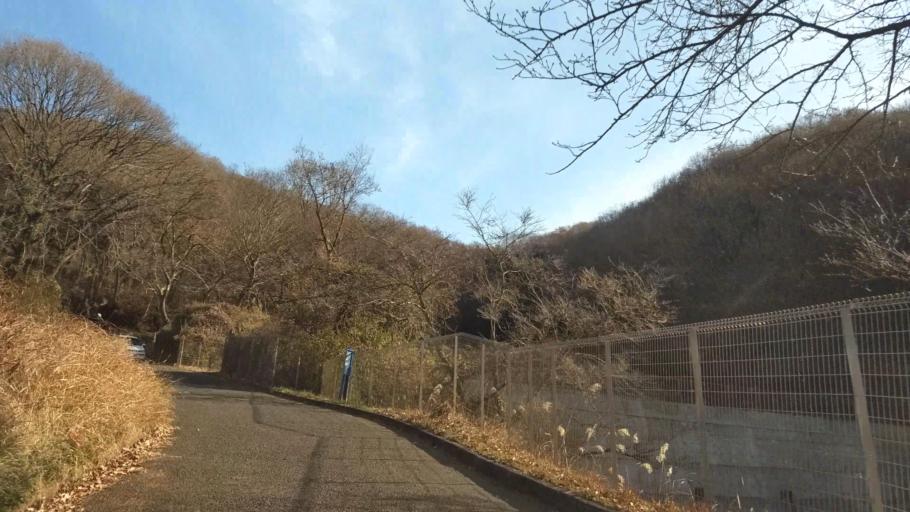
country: JP
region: Kanagawa
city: Hadano
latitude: 35.3733
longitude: 139.2387
